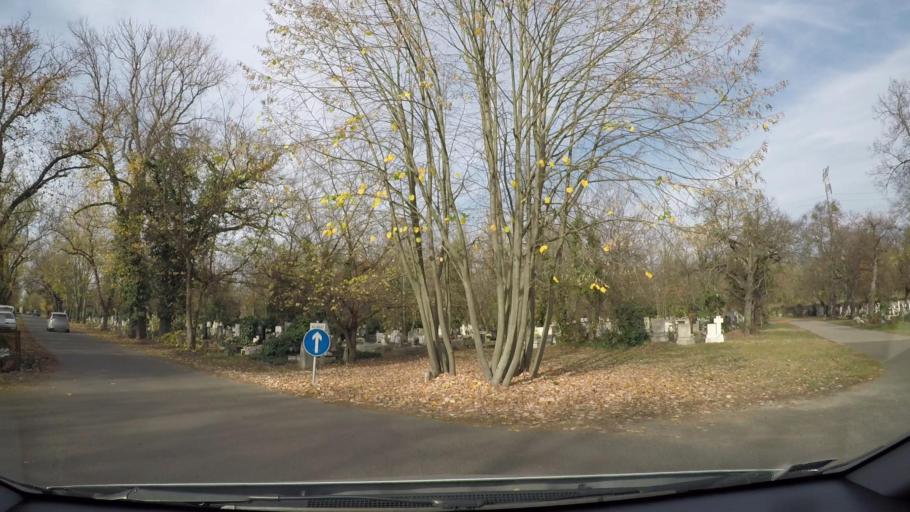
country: HU
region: Budapest
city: Budapest X. keruelet
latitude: 47.4753
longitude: 19.1851
